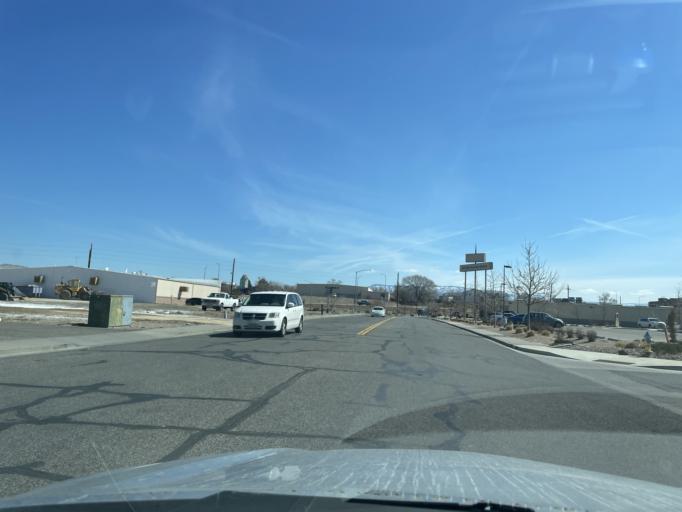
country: US
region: Colorado
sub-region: Mesa County
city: Grand Junction
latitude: 39.0729
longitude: -108.5758
